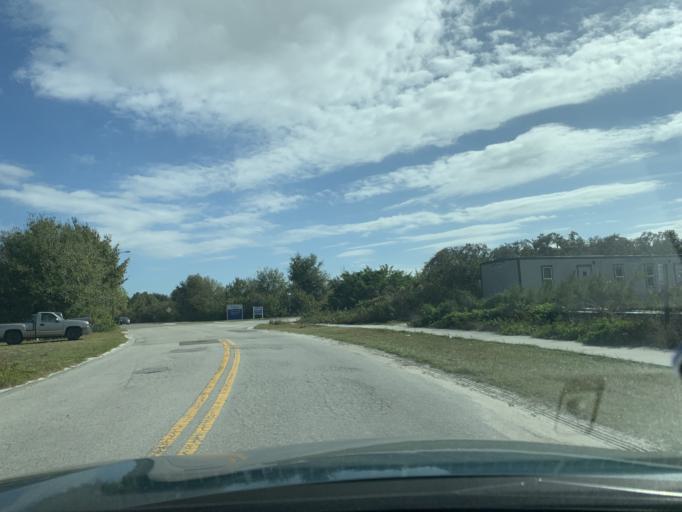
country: US
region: Florida
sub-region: Pasco County
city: Trinity
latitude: 28.1918
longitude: -82.6794
